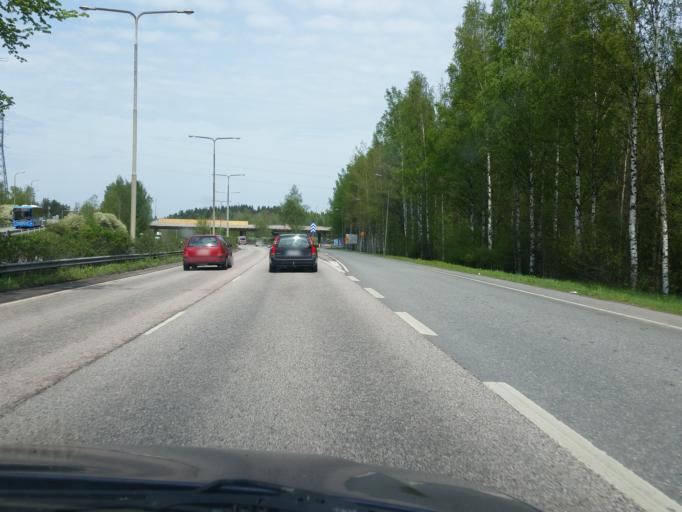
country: FI
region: Uusimaa
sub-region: Helsinki
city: Helsinki
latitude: 60.2171
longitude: 24.9080
